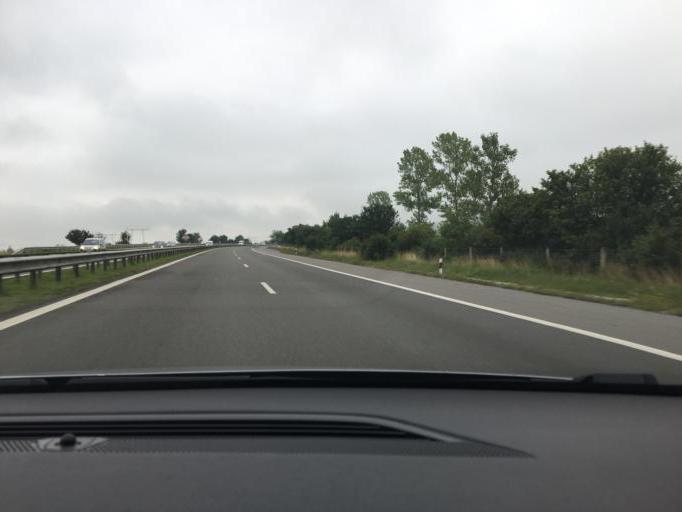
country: BG
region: Sofiya
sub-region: Obshtina Elin Pelin
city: Elin Pelin
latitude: 42.6114
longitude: 23.5386
